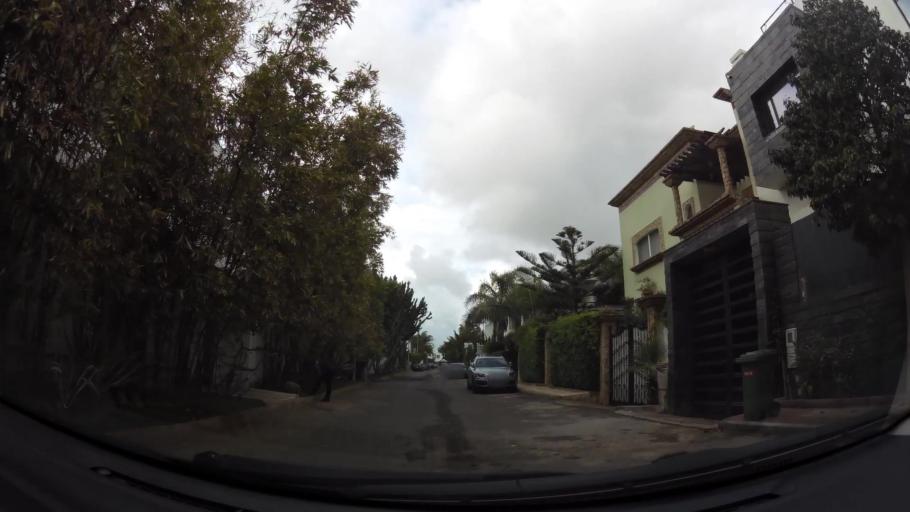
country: MA
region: Grand Casablanca
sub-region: Casablanca
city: Casablanca
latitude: 33.5850
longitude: -7.6824
